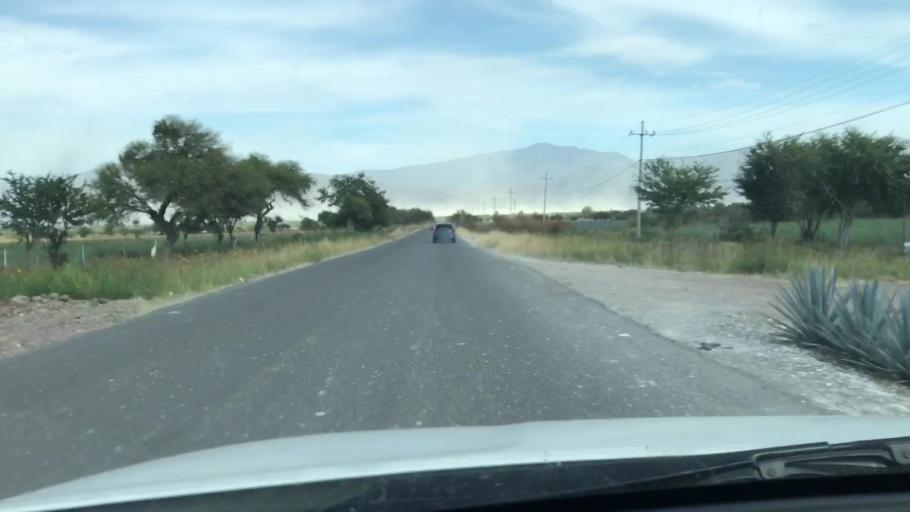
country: MX
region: Jalisco
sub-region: Zacoalco de Torres
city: Barranca de Otates (Barranca de Otatan)
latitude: 20.2824
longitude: -103.6188
